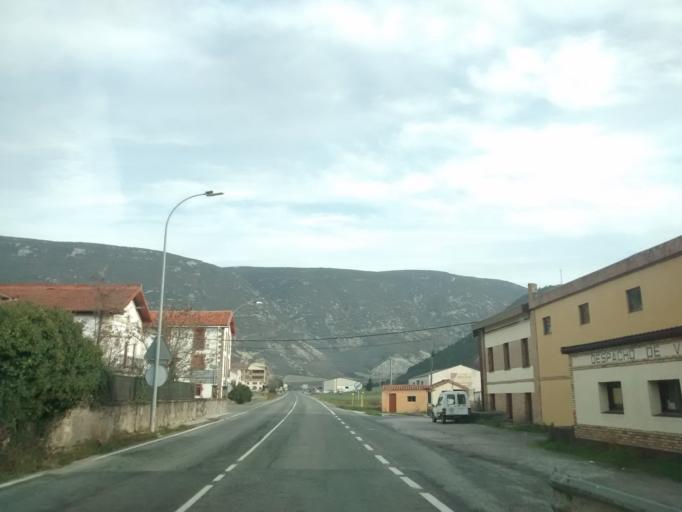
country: ES
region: Navarre
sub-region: Provincia de Navarra
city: Liedena
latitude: 42.6160
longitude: -1.2763
